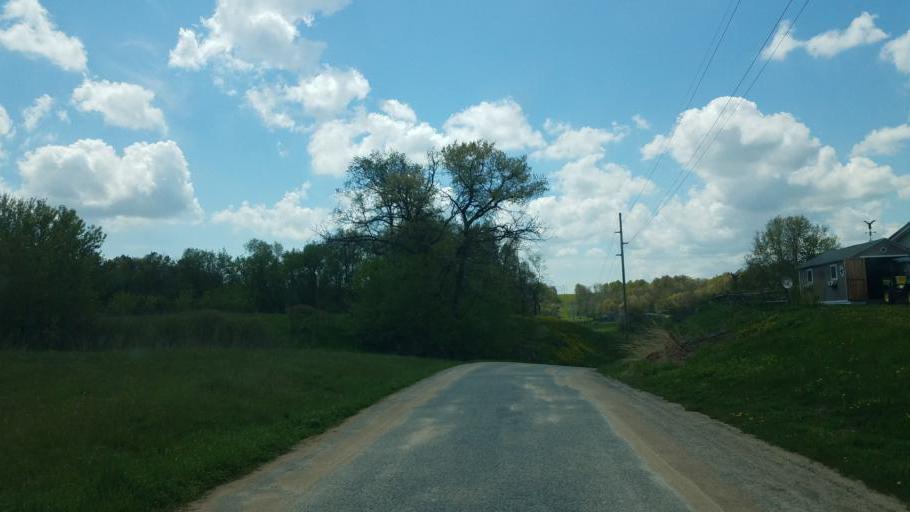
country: US
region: Wisconsin
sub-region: Vernon County
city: Hillsboro
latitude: 43.6829
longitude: -90.3324
